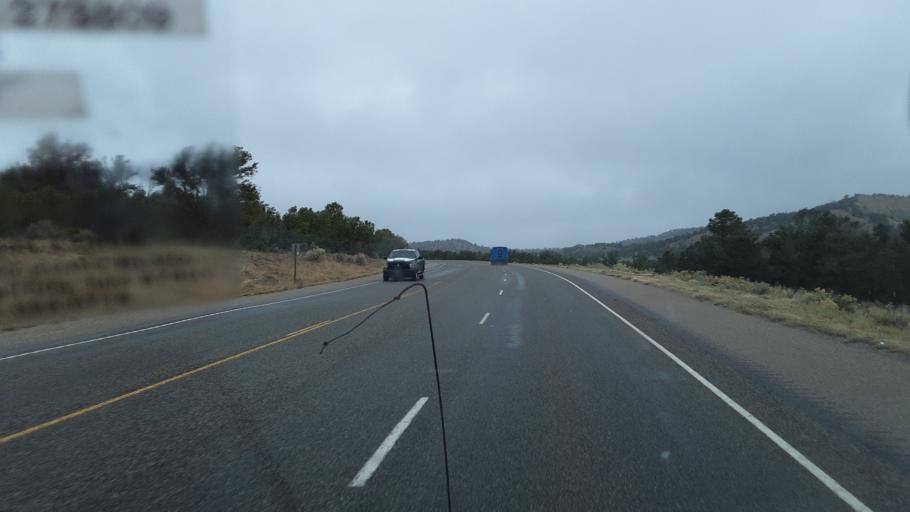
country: US
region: New Mexico
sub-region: Rio Arriba County
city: Tierra Amarilla
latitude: 36.4533
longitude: -106.4768
